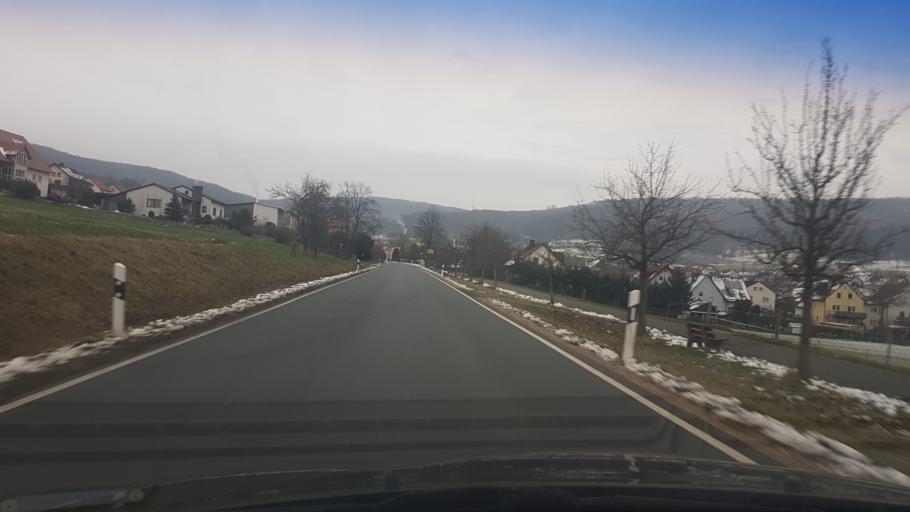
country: DE
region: Bavaria
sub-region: Upper Franconia
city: Litzendorf
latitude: 49.9023
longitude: 11.0265
